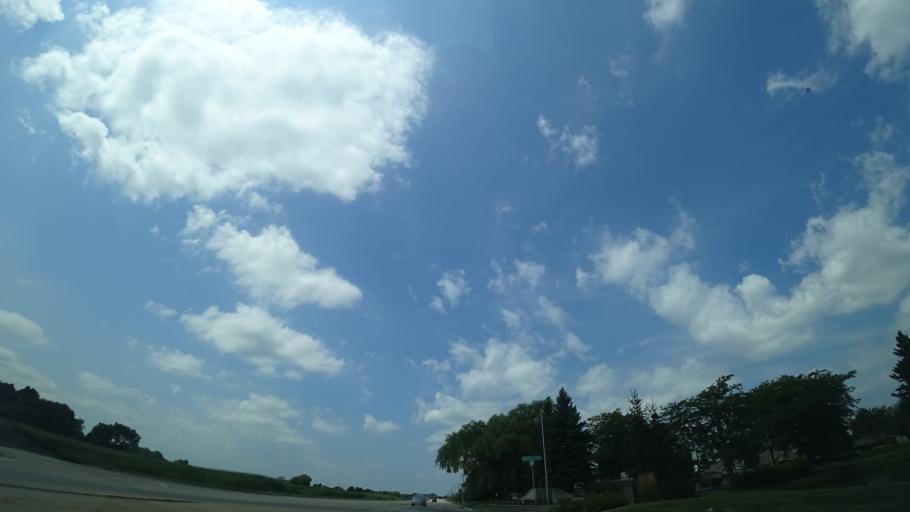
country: US
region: Illinois
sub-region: Will County
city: Frankfort Square
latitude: 41.5269
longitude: -87.7778
